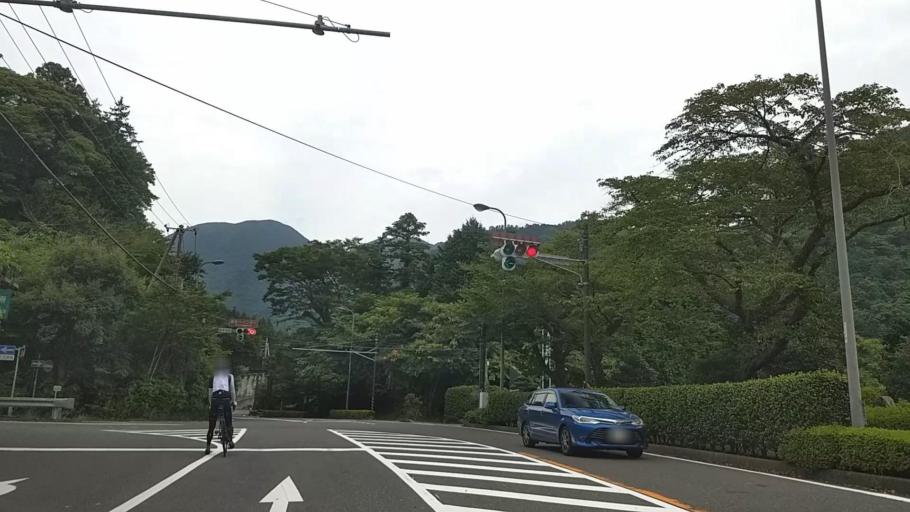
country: JP
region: Kanagawa
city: Hakone
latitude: 35.2219
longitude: 139.0801
